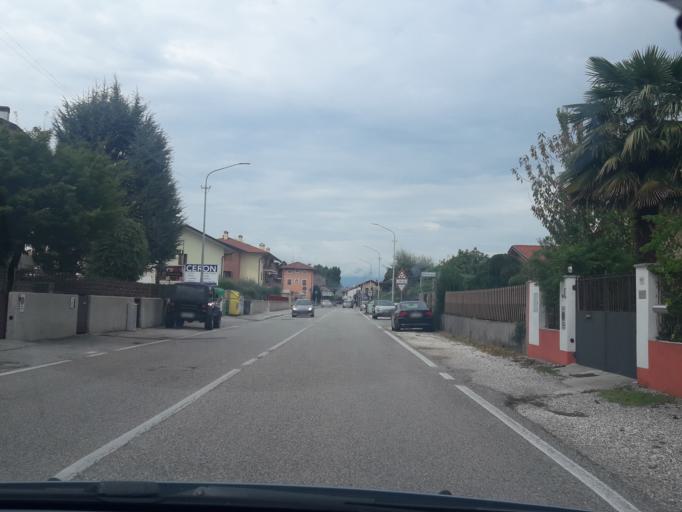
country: IT
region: Friuli Venezia Giulia
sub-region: Provincia di Udine
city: Udine
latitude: 46.0398
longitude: 13.2557
